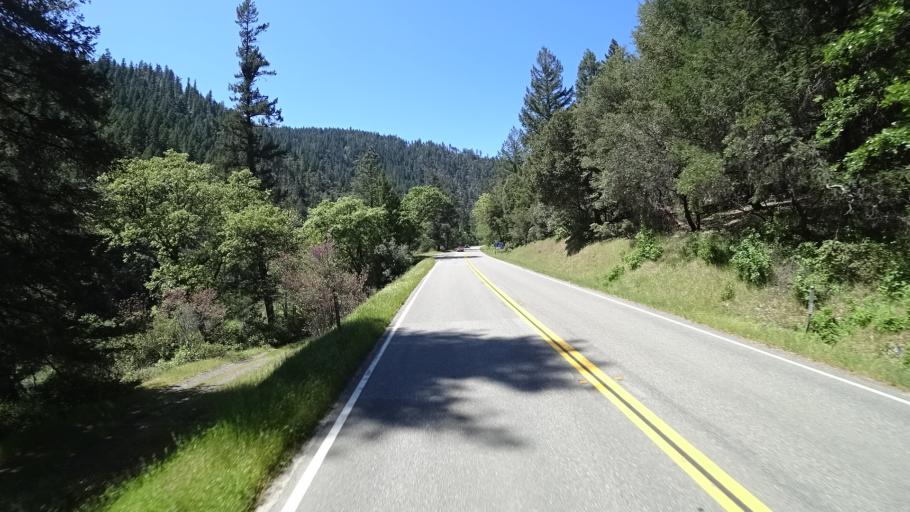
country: US
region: California
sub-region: Trinity County
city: Hayfork
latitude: 40.7504
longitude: -123.2778
